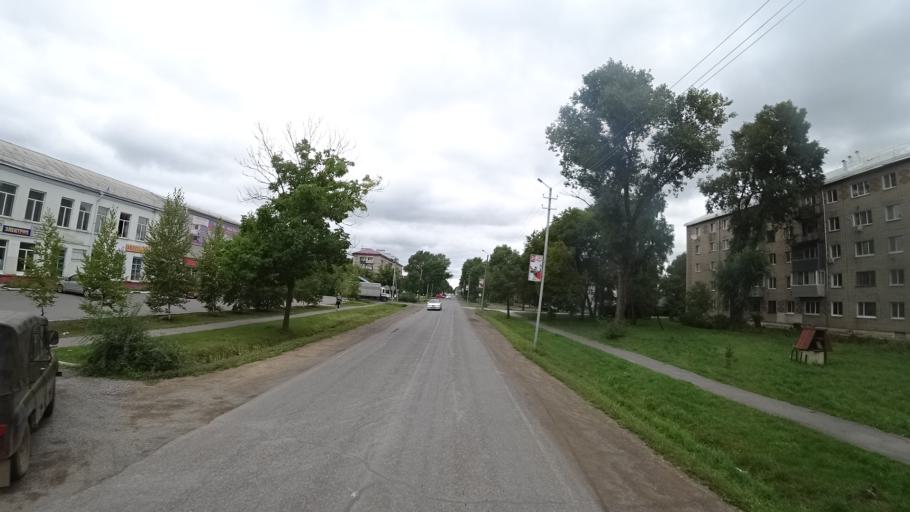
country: RU
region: Primorskiy
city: Chernigovka
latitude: 44.3413
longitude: 132.5785
